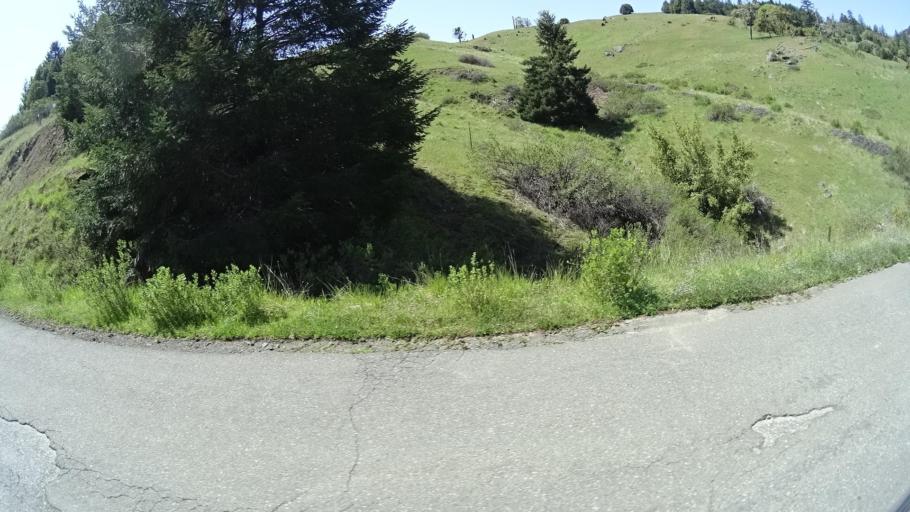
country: US
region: California
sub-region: Humboldt County
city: Redway
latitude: 40.1101
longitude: -123.6706
